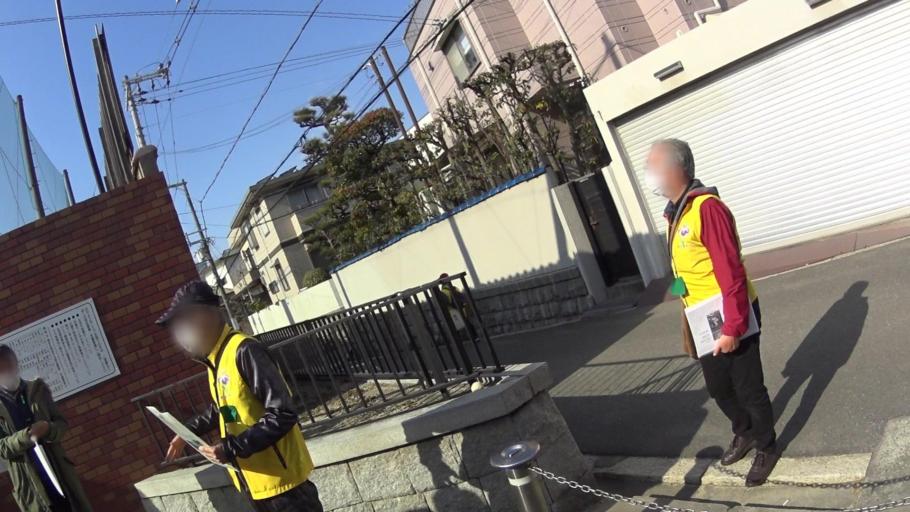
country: JP
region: Osaka
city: Sakai
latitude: 34.6247
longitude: 135.4968
